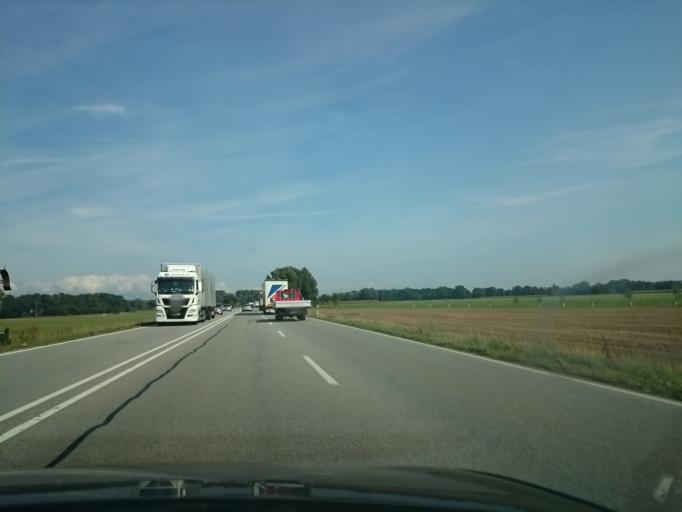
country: DE
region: Bavaria
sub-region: Upper Bavaria
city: Pornbach
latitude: 48.6270
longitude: 11.4447
